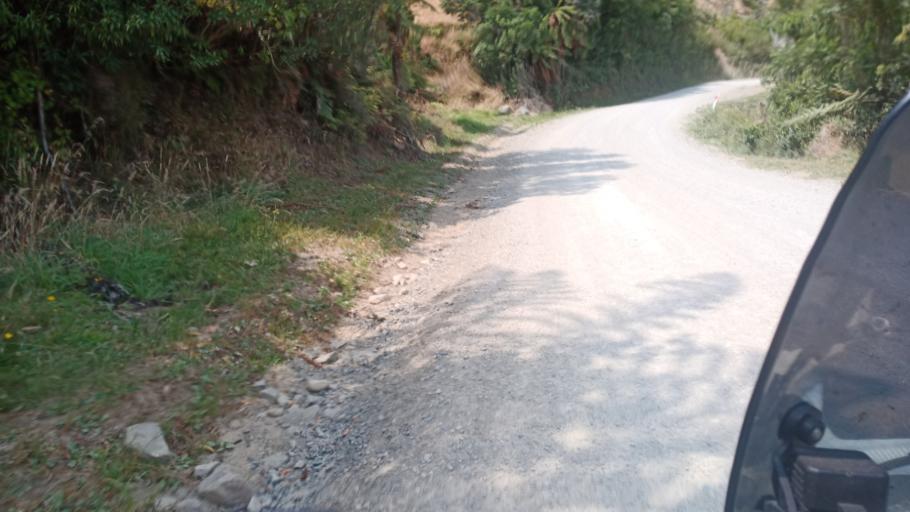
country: NZ
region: Bay of Plenty
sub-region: Opotiki District
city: Opotiki
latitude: -37.6556
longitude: 178.1378
